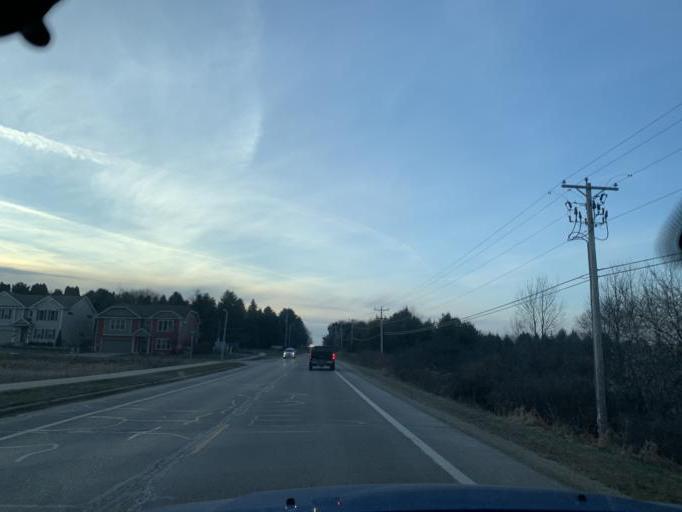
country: US
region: Wisconsin
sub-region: Dane County
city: Verona
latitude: 43.0457
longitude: -89.5459
